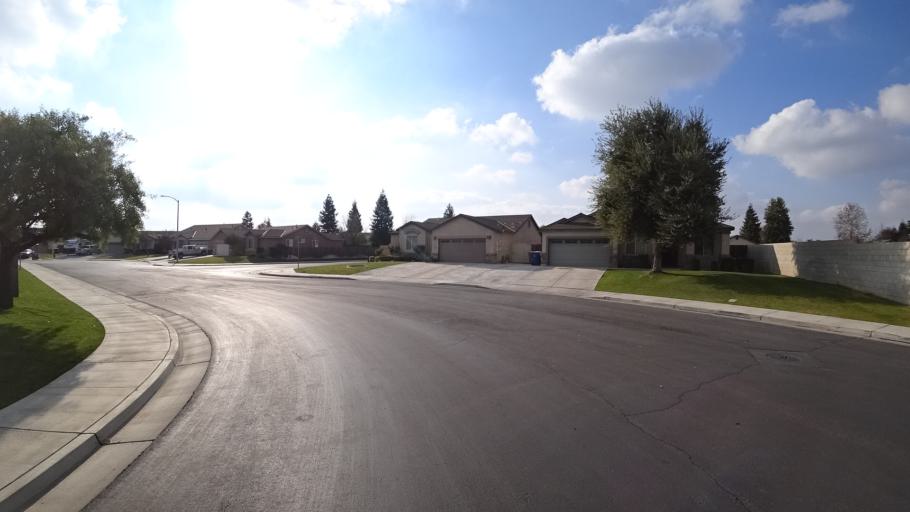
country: US
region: California
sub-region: Kern County
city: Greenacres
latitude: 35.3047
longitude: -119.1049
